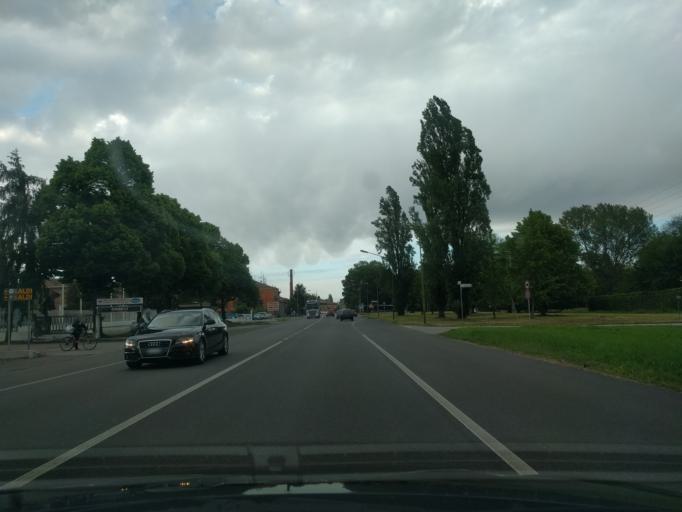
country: IT
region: Veneto
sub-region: Provincia di Rovigo
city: Santa Maria Maddalena
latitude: 44.8753
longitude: 11.6037
